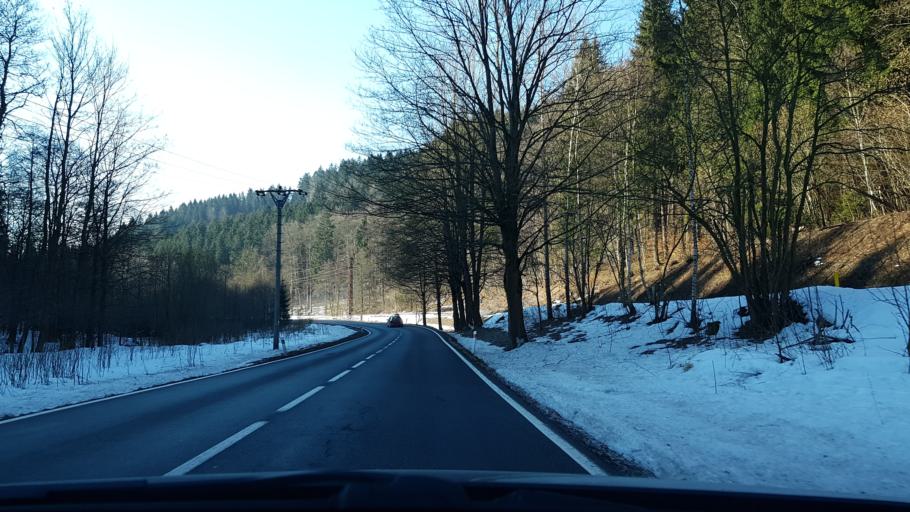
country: CZ
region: Olomoucky
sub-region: Okres Sumperk
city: Stare Mesto
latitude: 50.1256
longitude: 17.0091
